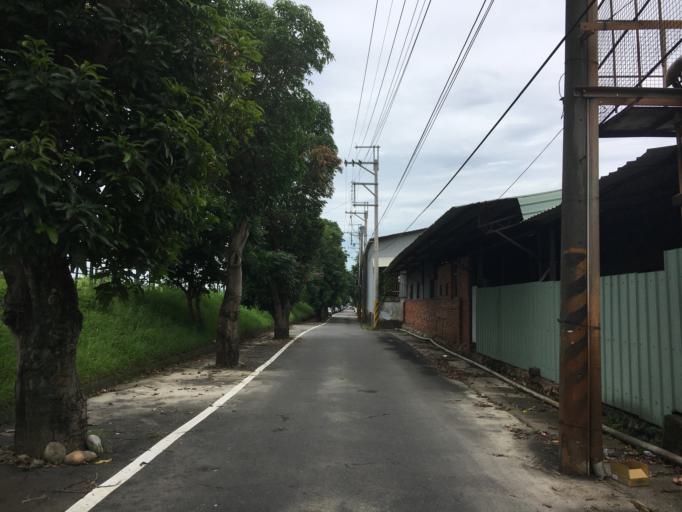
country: TW
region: Taiwan
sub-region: Taichung City
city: Taichung
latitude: 24.0849
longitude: 120.7179
